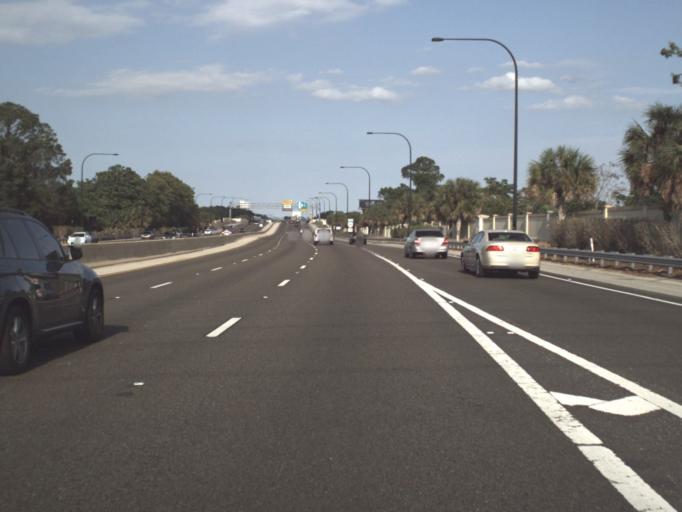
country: US
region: Florida
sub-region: Orange County
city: Pine Hills
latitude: 28.5482
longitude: -81.4538
